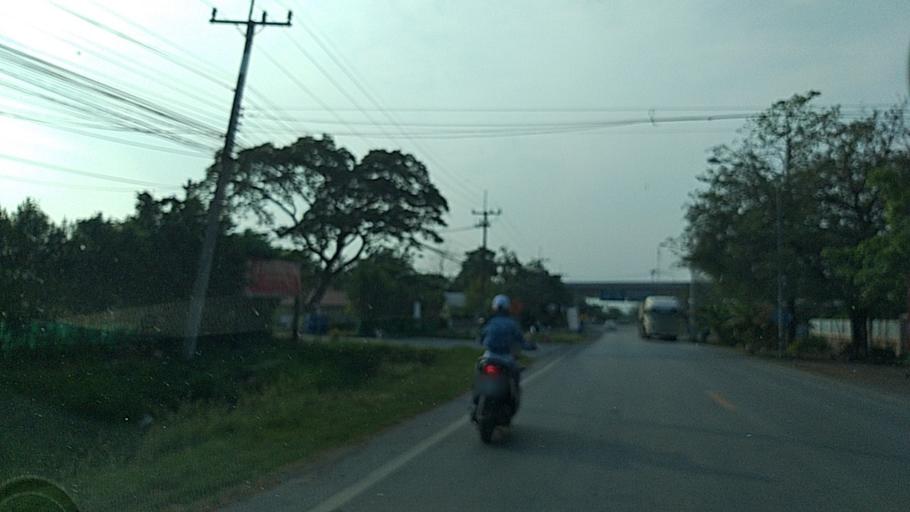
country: TH
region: Sara Buri
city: Saraburi
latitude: 14.4637
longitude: 100.9415
